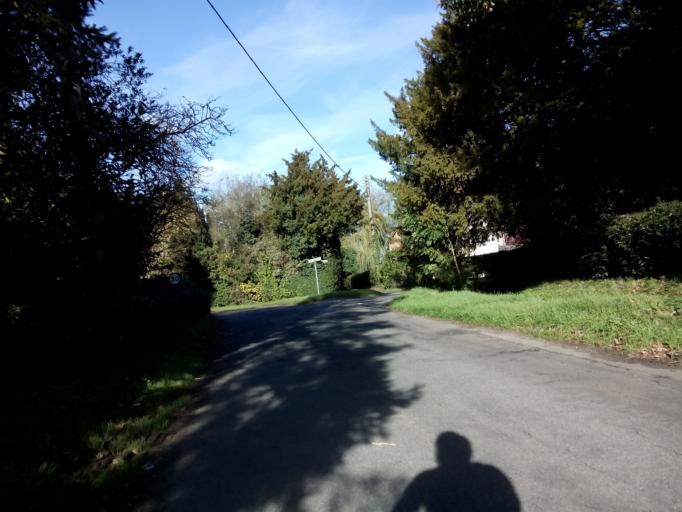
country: GB
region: England
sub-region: Suffolk
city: Capel Saint Mary
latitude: 52.0383
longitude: 1.0487
